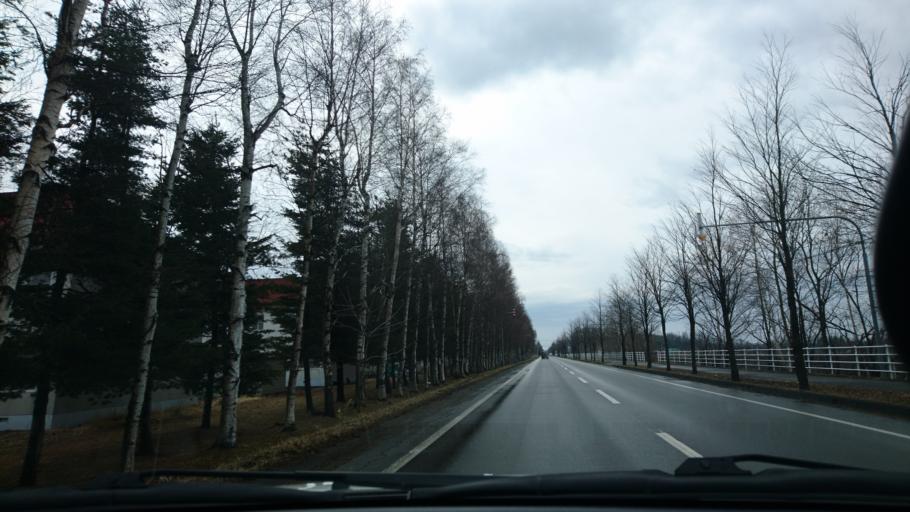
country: JP
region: Hokkaido
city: Otofuke
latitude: 42.9944
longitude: 143.1889
